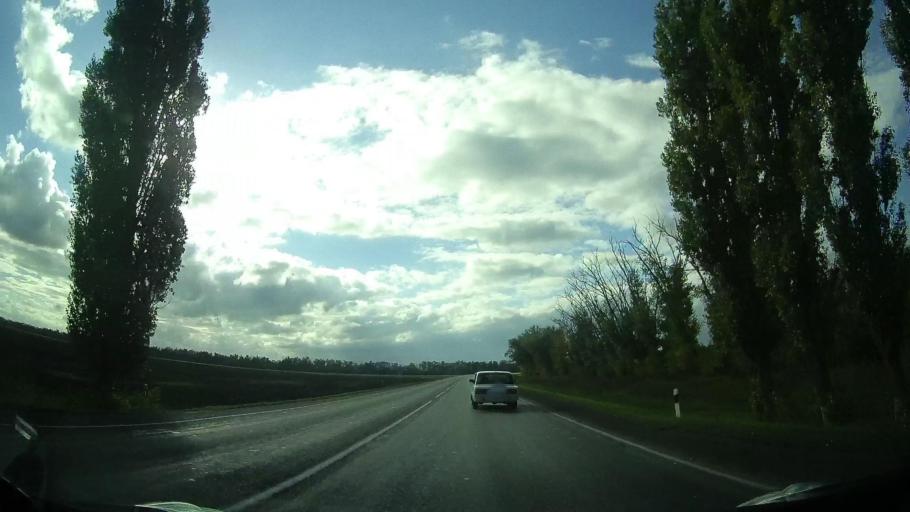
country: RU
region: Rostov
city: Tselina
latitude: 46.5305
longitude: 40.9541
